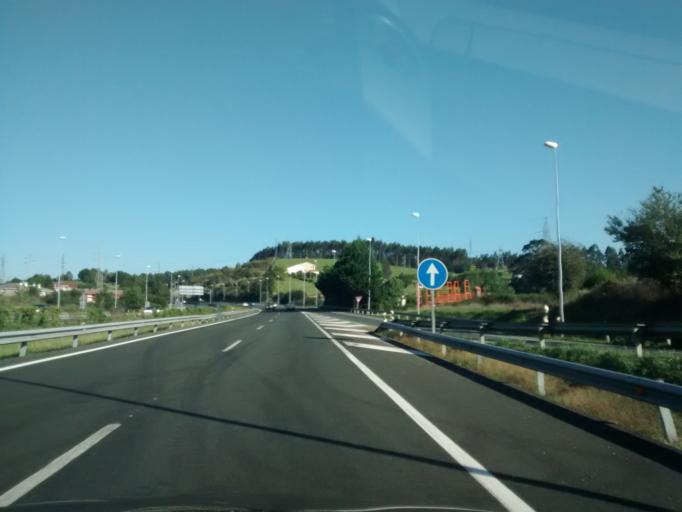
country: ES
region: Cantabria
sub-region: Provincia de Cantabria
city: Reocin
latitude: 43.3543
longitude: -4.0922
